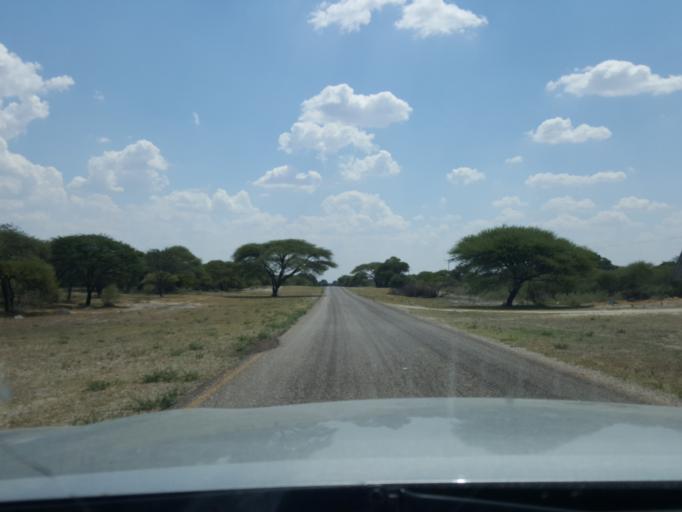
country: BW
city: Tsau
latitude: -20.1873
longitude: 22.4734
